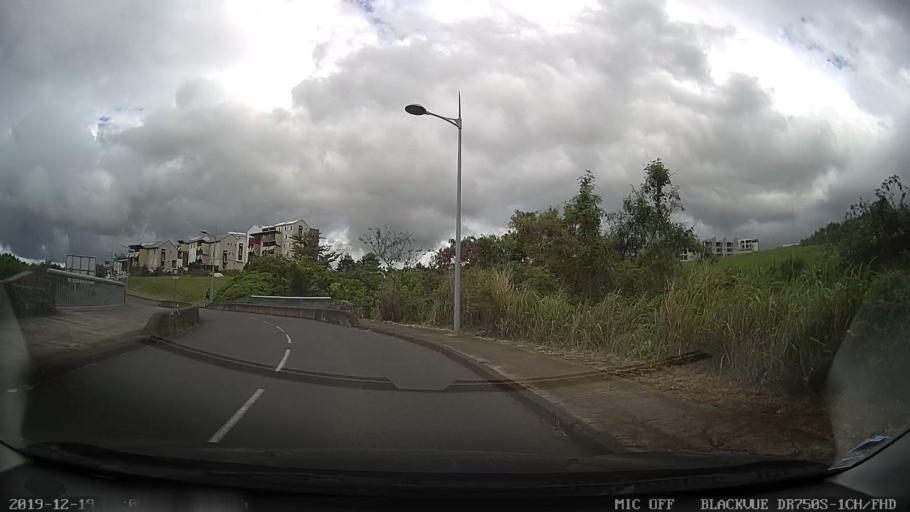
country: RE
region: Reunion
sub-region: Reunion
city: Sainte-Marie
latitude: -20.9181
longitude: 55.5263
